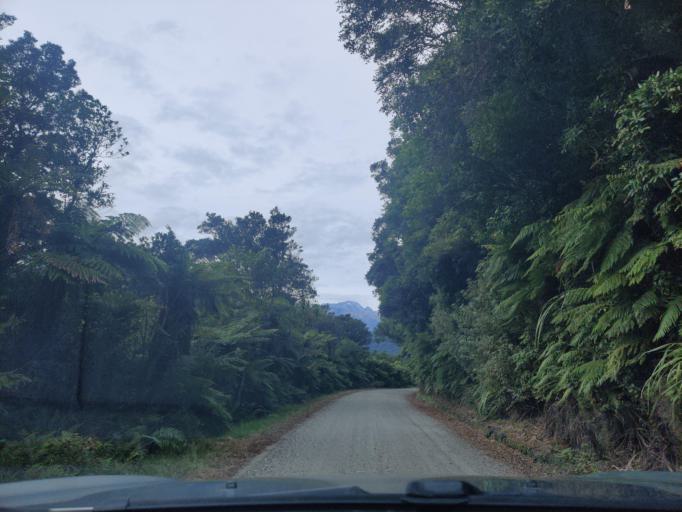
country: NZ
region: West Coast
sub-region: Westland District
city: Hokitika
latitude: -43.2898
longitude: 170.4052
